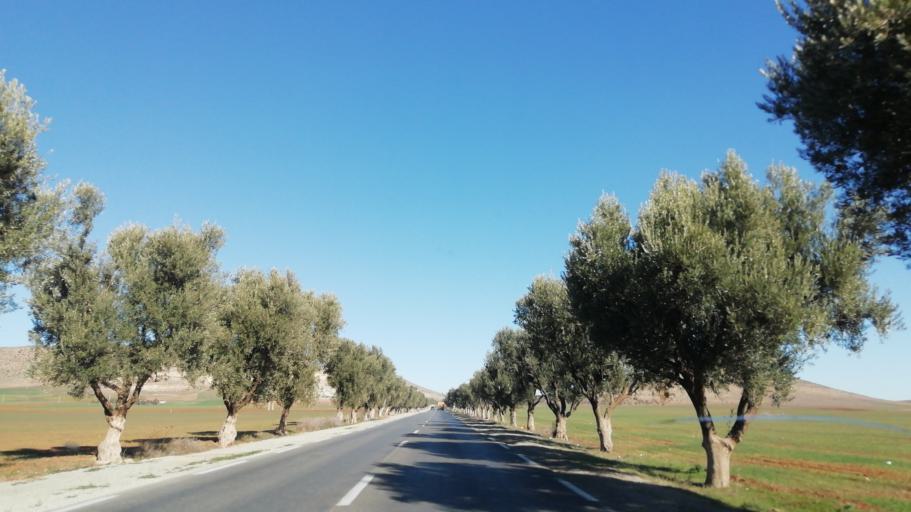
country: DZ
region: Mascara
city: Mascara
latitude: 35.2283
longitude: 0.1149
